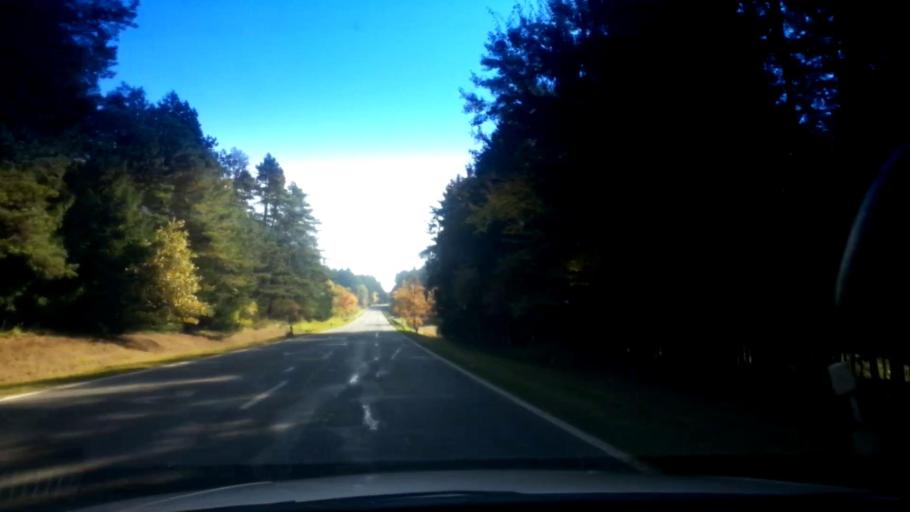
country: DE
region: Bavaria
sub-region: Upper Franconia
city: Stadelhofen
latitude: 49.9785
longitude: 11.2429
